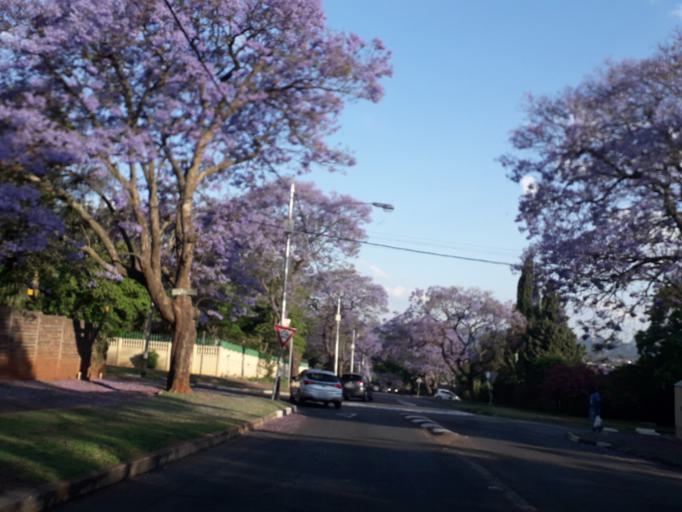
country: ZA
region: Gauteng
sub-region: City of Johannesburg Metropolitan Municipality
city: Johannesburg
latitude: -26.1351
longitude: 27.9992
